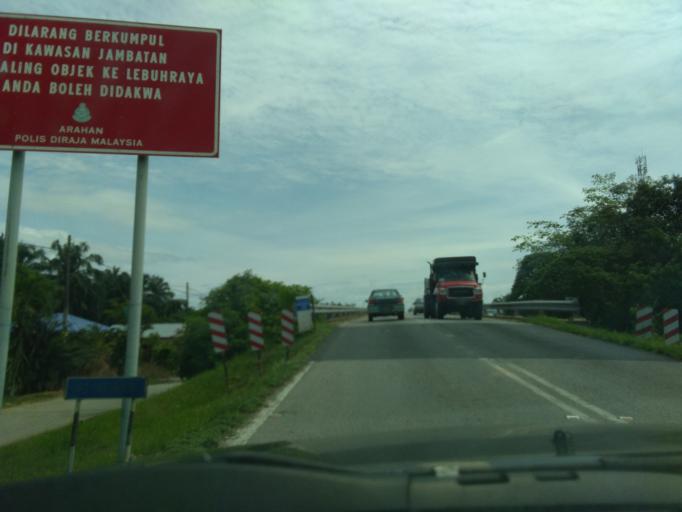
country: MY
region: Perak
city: Bagan Serai
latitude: 5.0617
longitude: 100.5947
